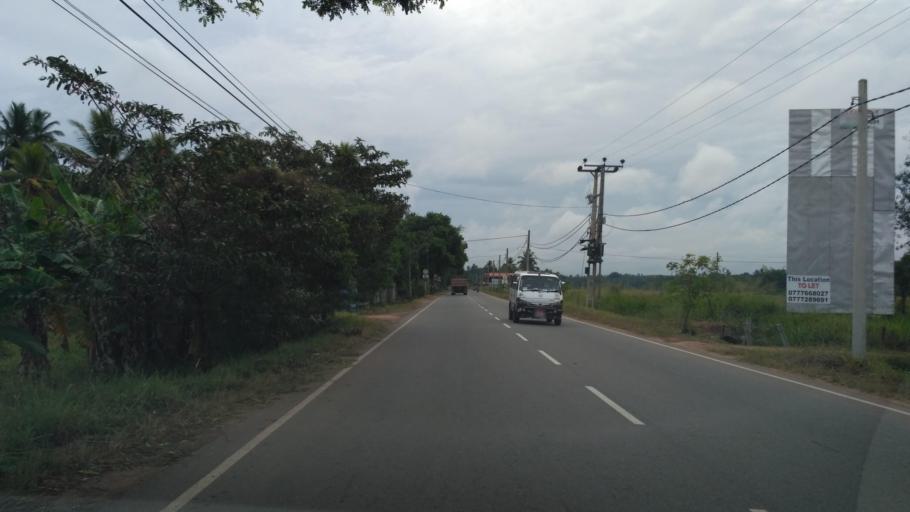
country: LK
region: North Western
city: Kuliyapitiya
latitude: 7.3270
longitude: 80.0297
